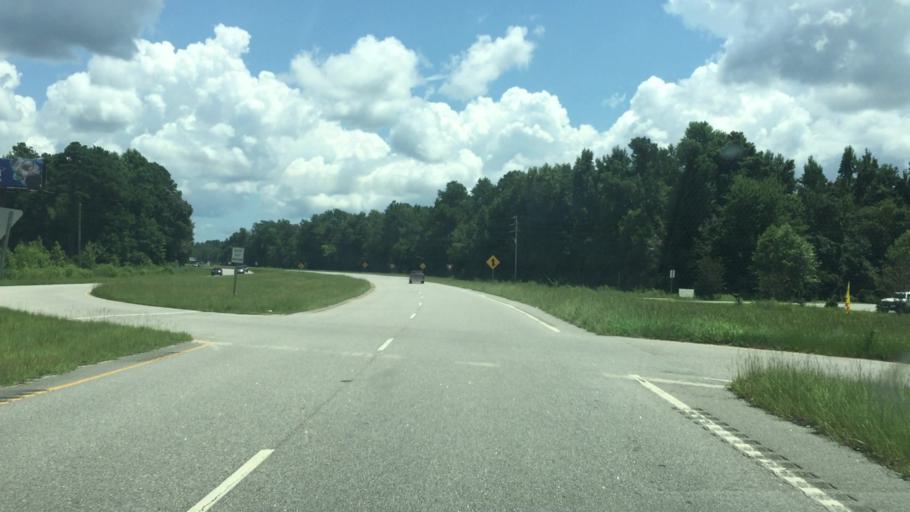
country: US
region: South Carolina
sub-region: Horry County
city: Loris
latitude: 34.0181
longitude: -78.7935
